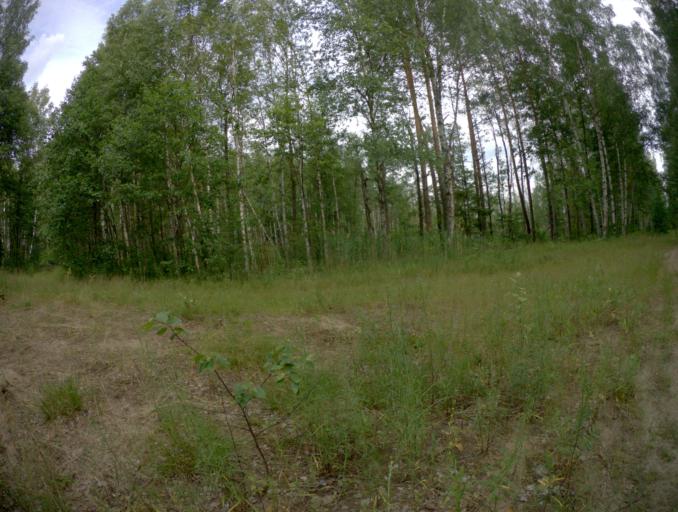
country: RU
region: Vladimir
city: Gorokhovets
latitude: 56.2947
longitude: 42.6499
